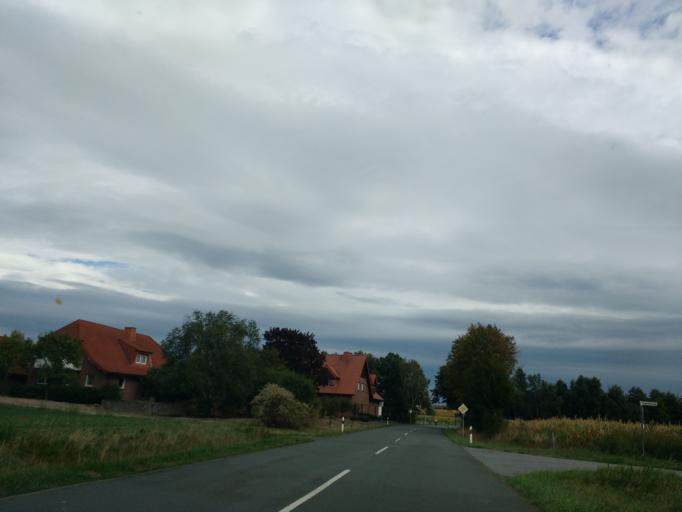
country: DE
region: North Rhine-Westphalia
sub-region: Regierungsbezirk Detmold
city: Delbruck
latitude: 51.8048
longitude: 8.5253
